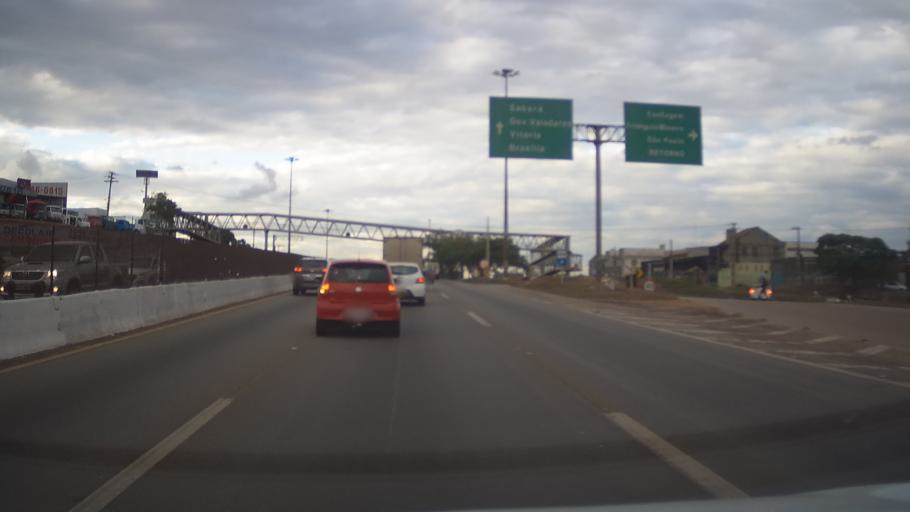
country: BR
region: Minas Gerais
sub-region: Contagem
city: Contagem
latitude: -19.9459
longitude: -44.0079
